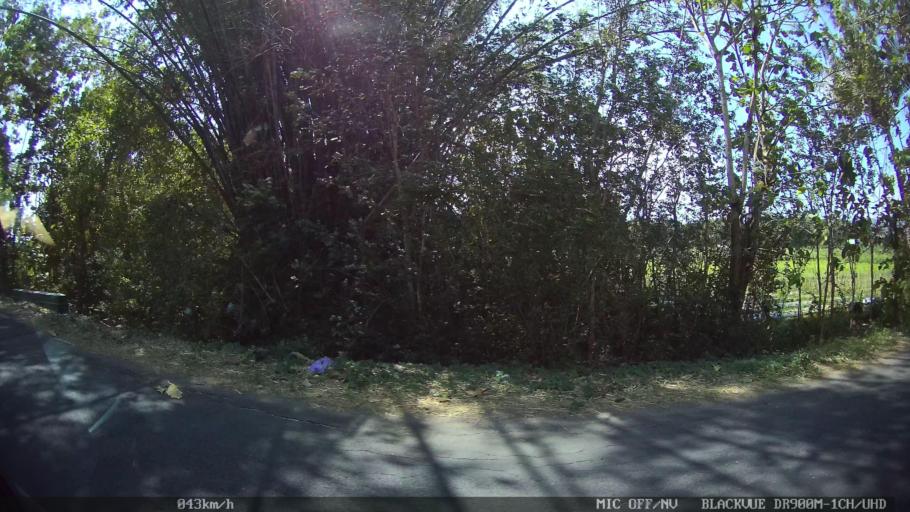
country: ID
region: Daerah Istimewa Yogyakarta
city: Pundong
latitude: -7.9568
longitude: 110.3686
